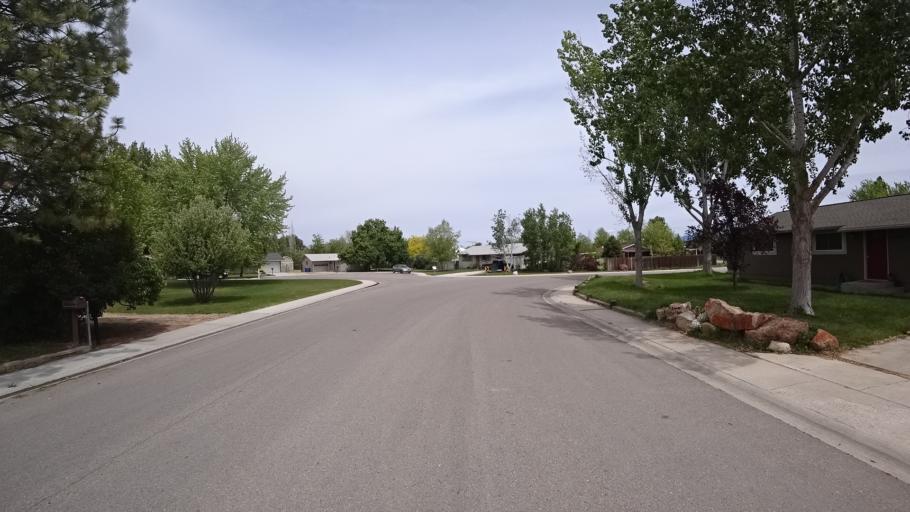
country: US
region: Idaho
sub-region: Ada County
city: Meridian
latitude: 43.5436
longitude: -116.3252
